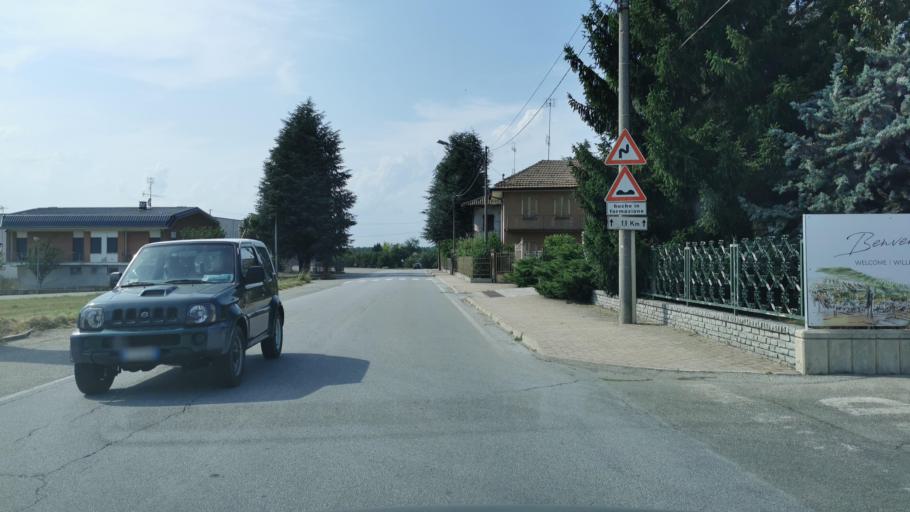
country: IT
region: Piedmont
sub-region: Provincia di Cuneo
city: Grinzane Cavour
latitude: 44.6408
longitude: 8.0017
